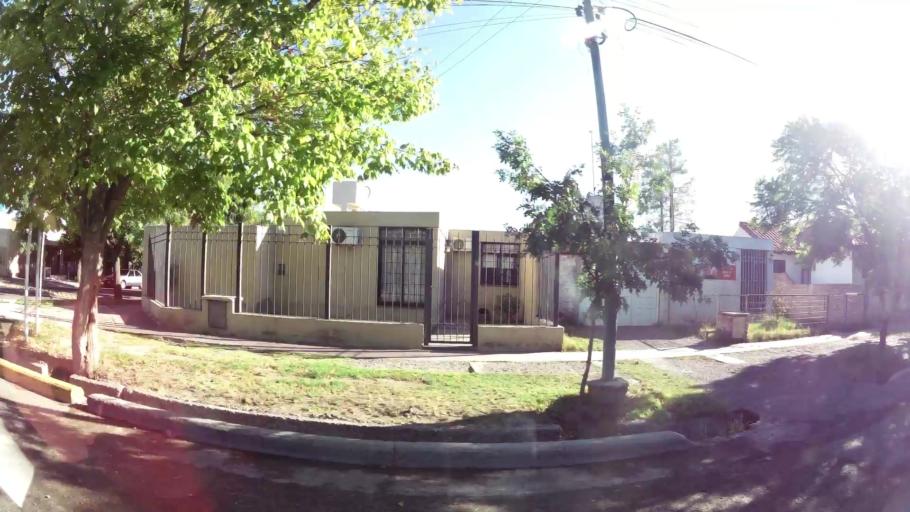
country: AR
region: Mendoza
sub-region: Departamento de Godoy Cruz
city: Godoy Cruz
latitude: -32.9310
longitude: -68.8336
